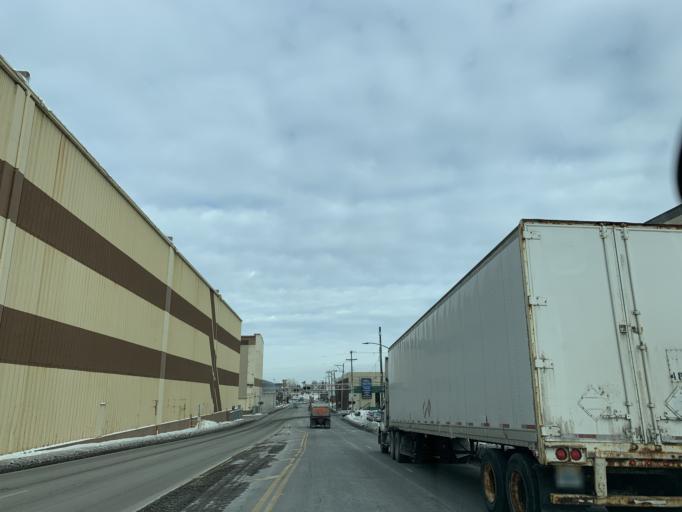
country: US
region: Minnesota
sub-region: Ramsey County
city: Falcon Heights
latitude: 44.9578
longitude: -93.1920
